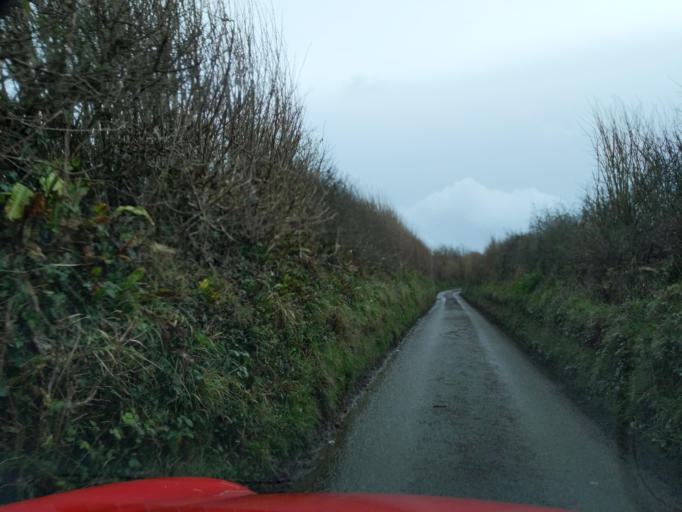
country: GB
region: England
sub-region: Cornwall
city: Duloe
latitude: 50.3557
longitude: -4.5164
